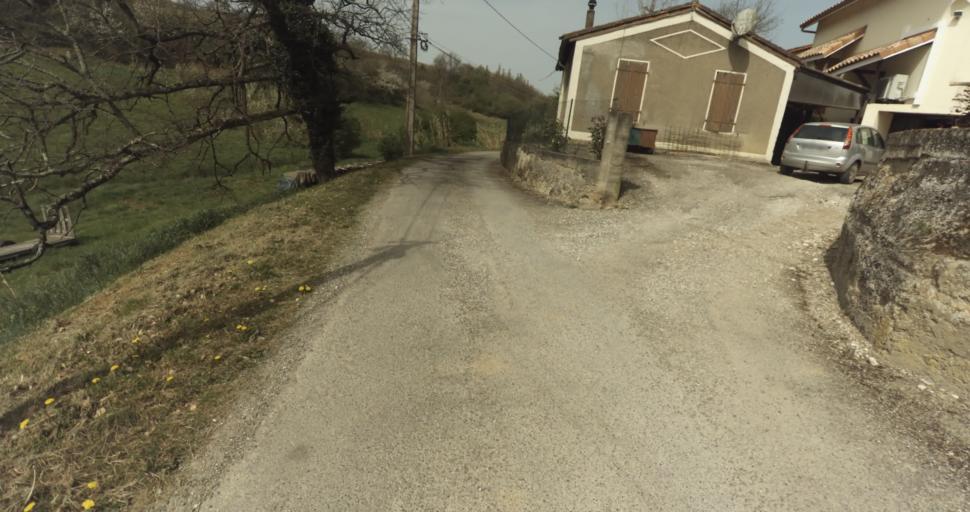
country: FR
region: Midi-Pyrenees
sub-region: Departement du Tarn-et-Garonne
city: Moissac
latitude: 44.1054
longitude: 1.0693
